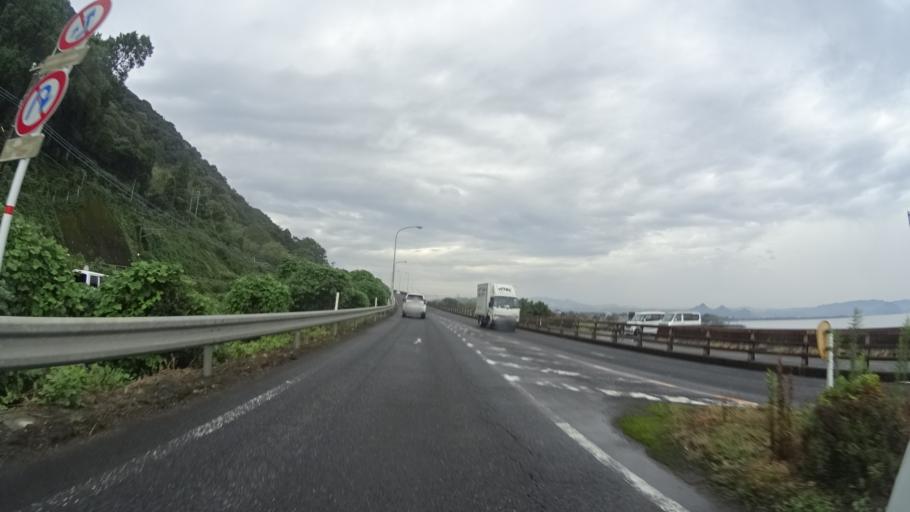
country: JP
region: Kagoshima
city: Kajiki
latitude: 31.6958
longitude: 130.6140
